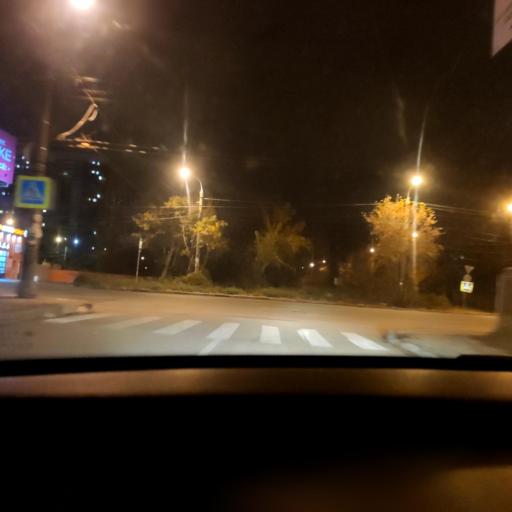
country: RU
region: Samara
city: Samara
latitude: 53.2141
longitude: 50.1882
